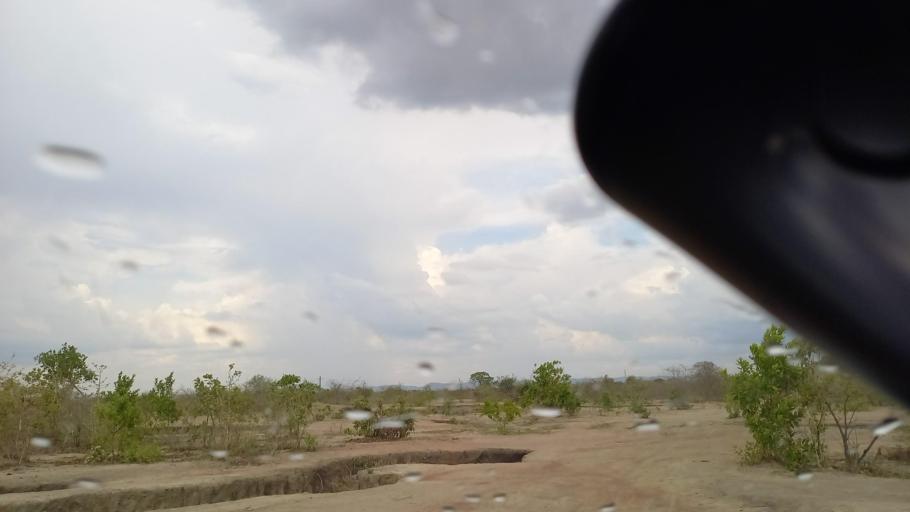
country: ZM
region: Lusaka
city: Kafue
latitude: -15.8552
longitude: 28.1154
